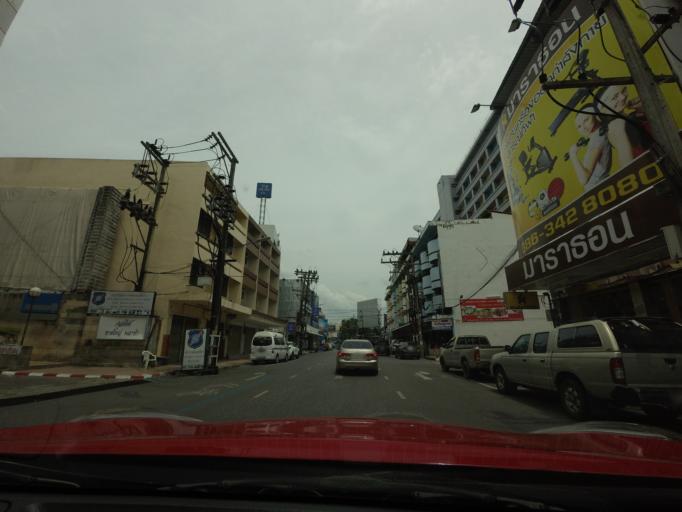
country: TH
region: Songkhla
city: Hat Yai
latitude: 6.9987
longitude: 100.4715
